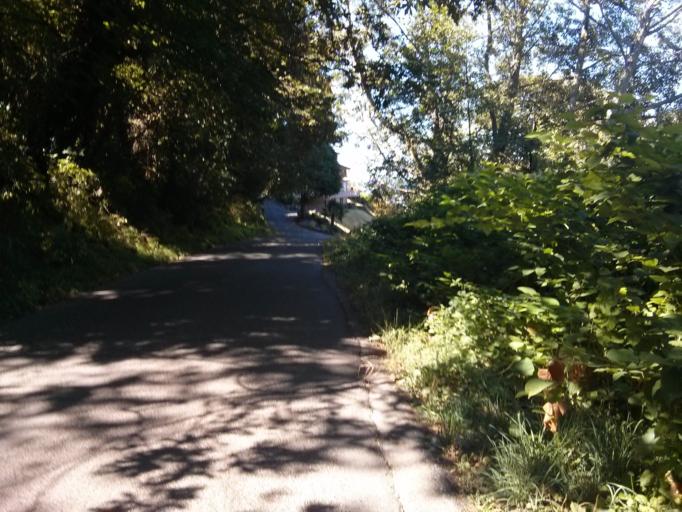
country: US
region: Washington
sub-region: King County
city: Seattle
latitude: 47.5870
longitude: -122.3939
